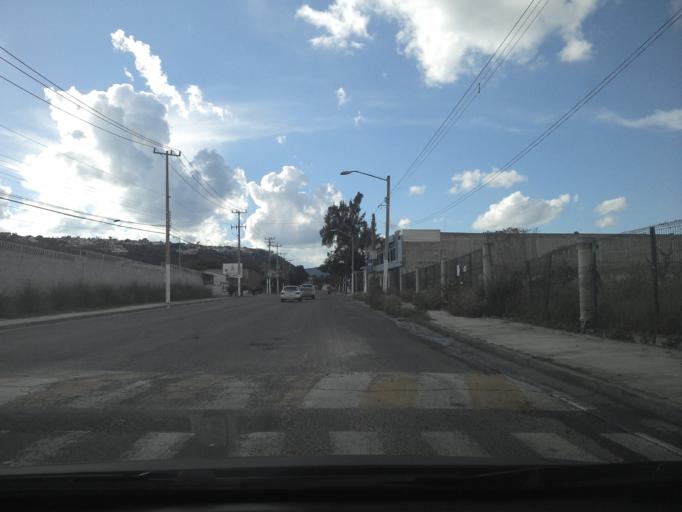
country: MX
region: Jalisco
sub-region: Tlajomulco de Zuniga
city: Palomar
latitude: 20.6172
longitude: -103.4485
